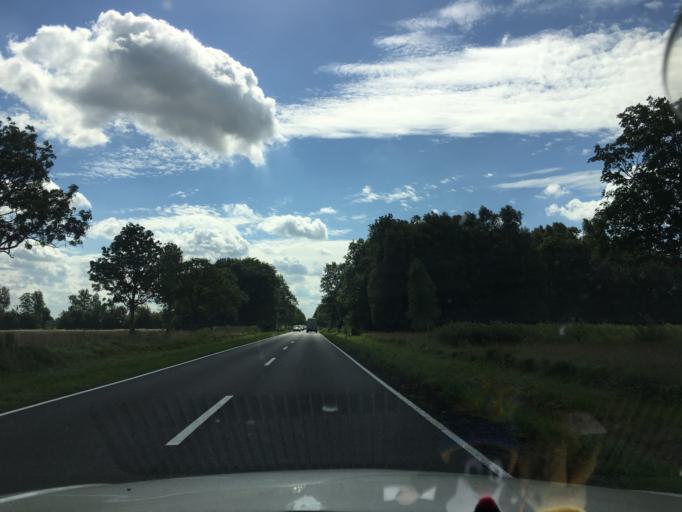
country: PL
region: West Pomeranian Voivodeship
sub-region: Powiat kamienski
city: Kamien Pomorski
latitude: 53.9454
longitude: 14.8060
